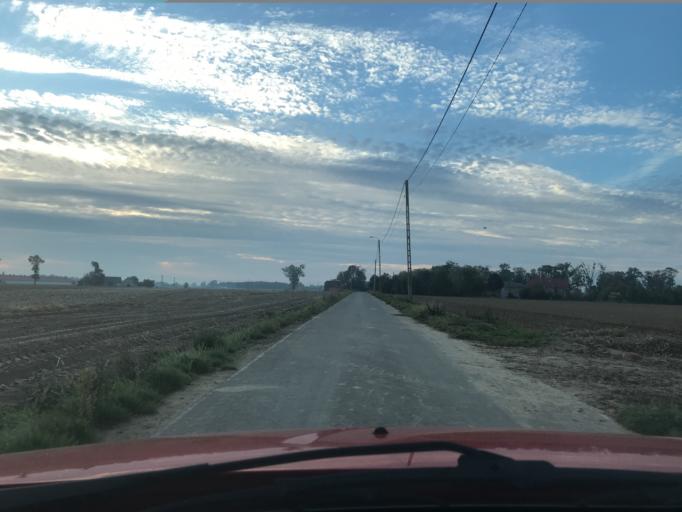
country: PL
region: Greater Poland Voivodeship
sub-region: Powiat ostrowski
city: Skalmierzyce
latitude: 51.7593
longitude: 17.9005
